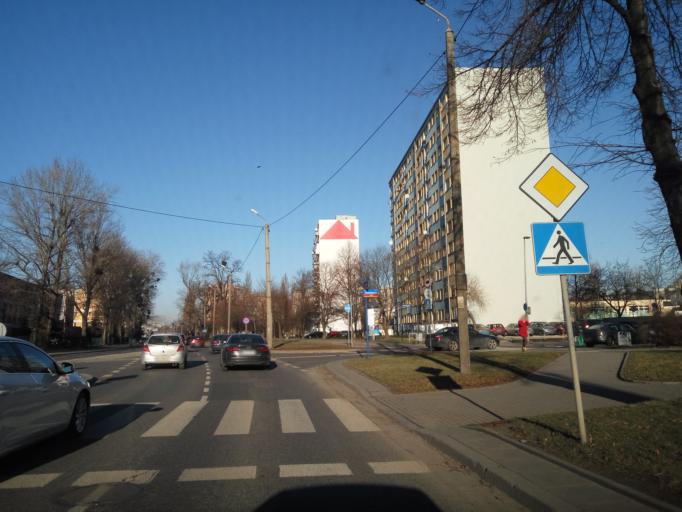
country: PL
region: Lower Silesian Voivodeship
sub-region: Powiat wroclawski
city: Wroclaw
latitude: 51.0861
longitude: 17.0354
